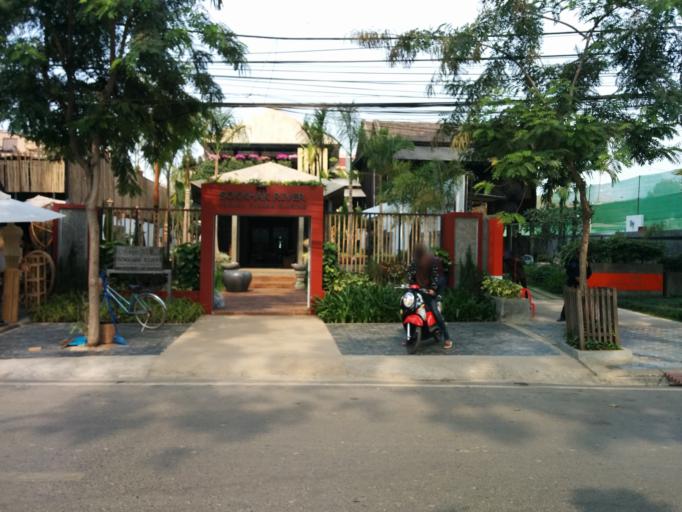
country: KH
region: Siem Reap
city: Siem Reap
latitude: 13.3559
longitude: 103.8578
